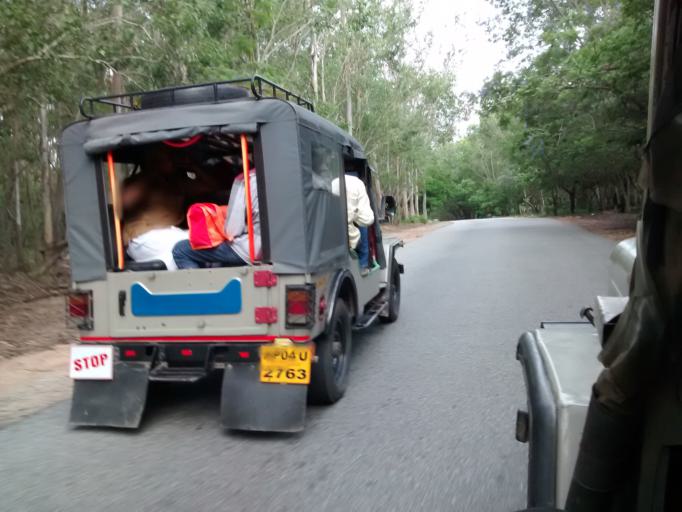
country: IN
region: Andhra Pradesh
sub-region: Chittoor
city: Tirumala
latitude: 13.7022
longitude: 79.3470
